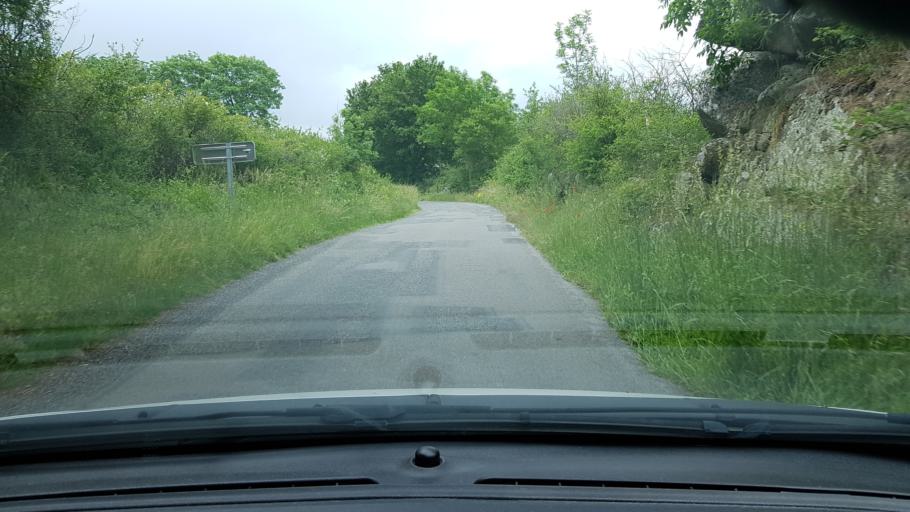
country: FR
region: Rhone-Alpes
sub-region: Departement du Rhone
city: Chassagny
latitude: 45.6059
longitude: 4.7113
